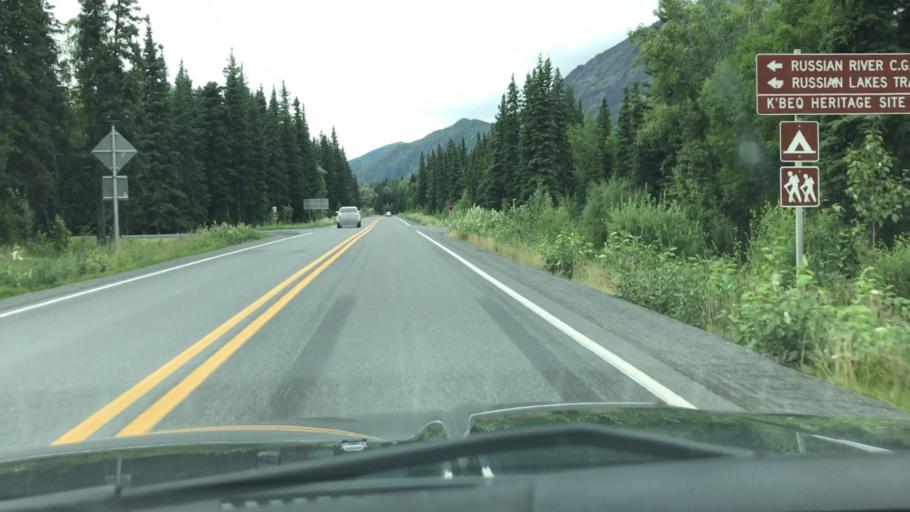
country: US
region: Alaska
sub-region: Kenai Peninsula Borough
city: Seward
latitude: 60.4828
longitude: -149.9364
